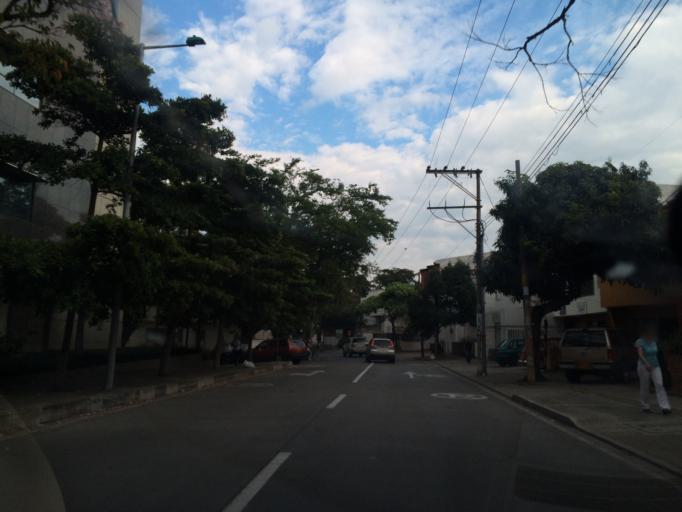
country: CO
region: Valle del Cauca
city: Cali
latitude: 3.4368
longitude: -76.5450
